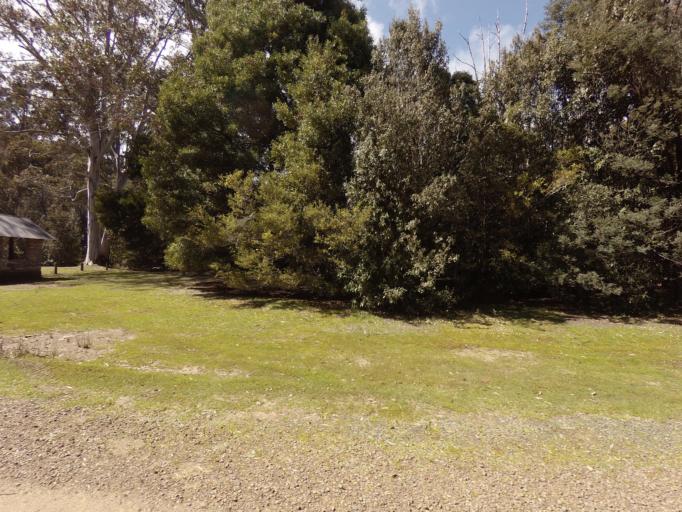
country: AU
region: Tasmania
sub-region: Derwent Valley
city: New Norfolk
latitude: -42.6816
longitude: 146.7190
